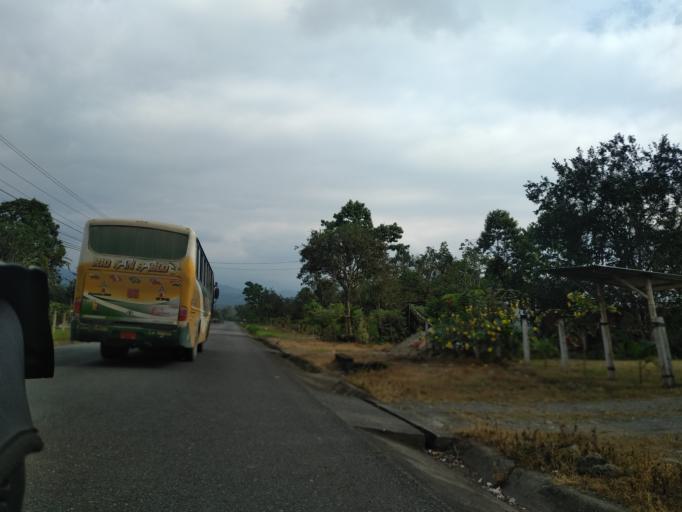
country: EC
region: Cotopaxi
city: La Mana
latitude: -0.8982
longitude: -79.1620
